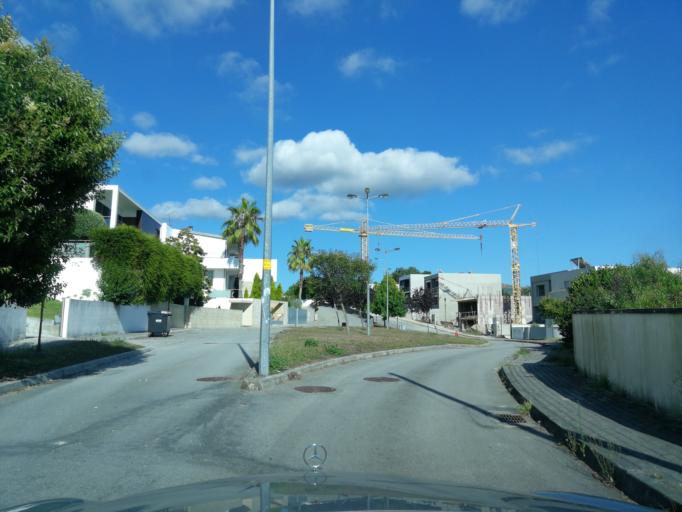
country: PT
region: Braga
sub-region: Braga
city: Adaufe
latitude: 41.5735
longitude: -8.3793
